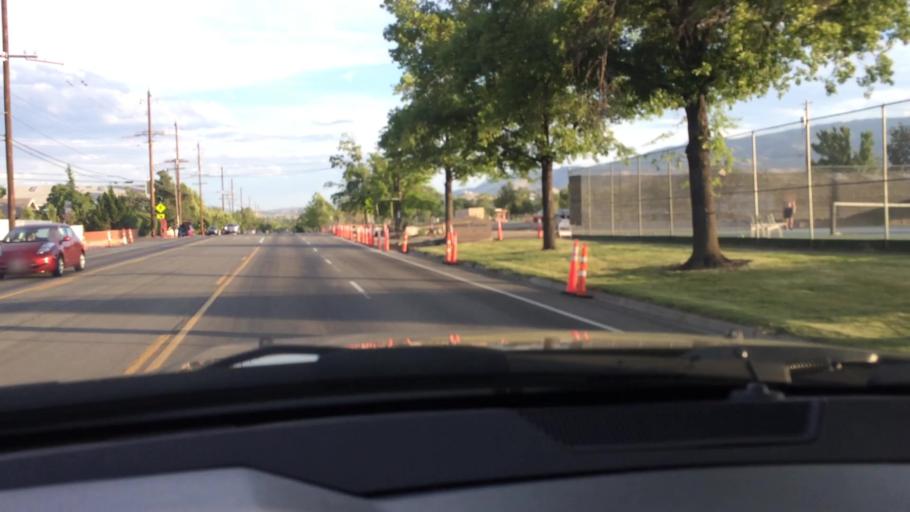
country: US
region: Nevada
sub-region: Washoe County
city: Reno
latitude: 39.4992
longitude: -119.8127
